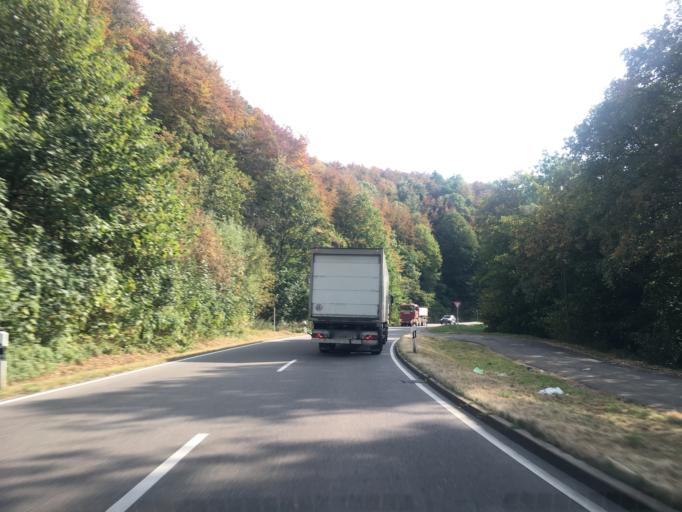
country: DE
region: Baden-Wuerttemberg
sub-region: Tuebingen Region
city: Pfullingen
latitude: 48.4174
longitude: 9.1817
